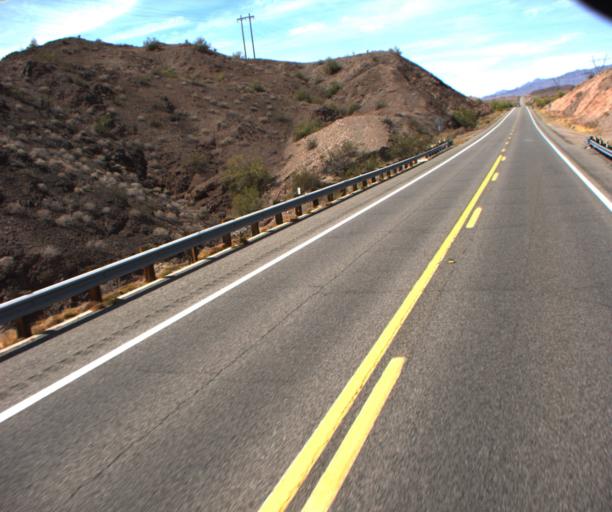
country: US
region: Arizona
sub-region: La Paz County
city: Cienega Springs
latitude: 34.3534
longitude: -114.1551
